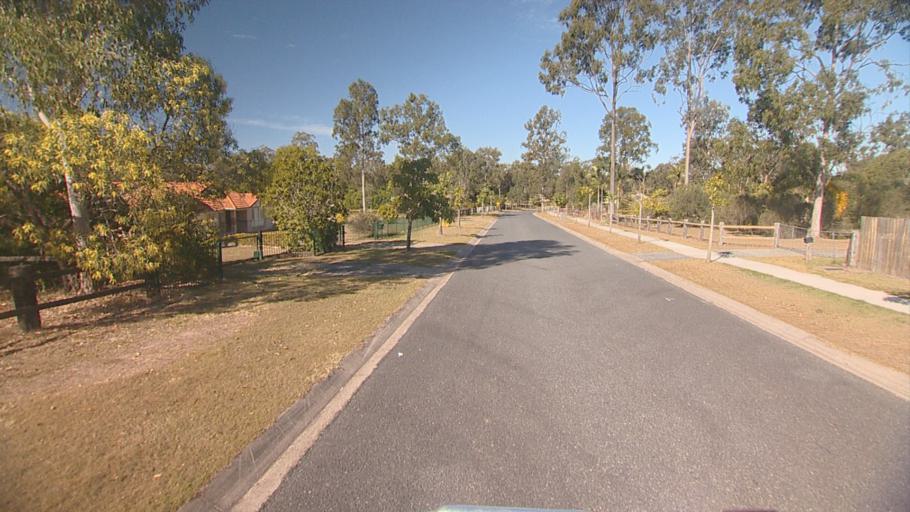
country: AU
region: Queensland
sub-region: Logan
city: North Maclean
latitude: -27.8075
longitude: 152.9612
